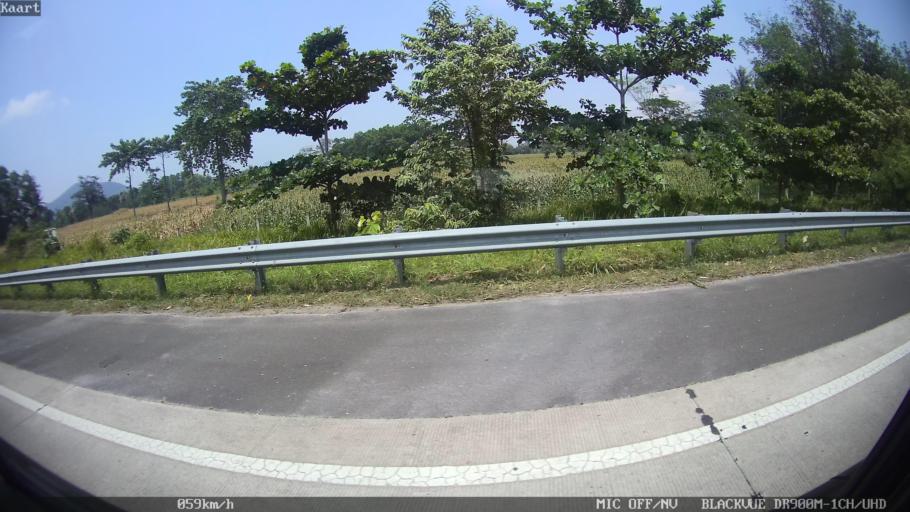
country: ID
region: Lampung
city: Kedaton
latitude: -5.3795
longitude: 105.3317
